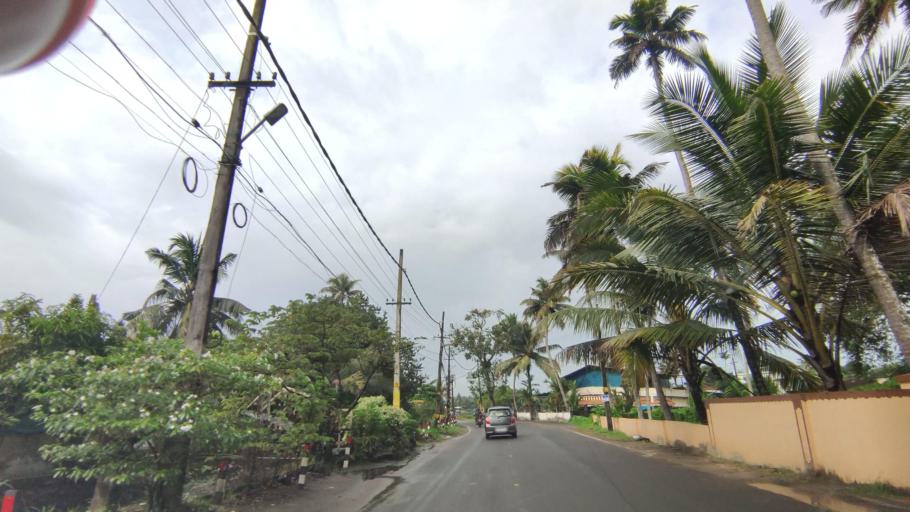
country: IN
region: Kerala
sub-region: Kottayam
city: Kottayam
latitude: 9.5772
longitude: 76.5009
